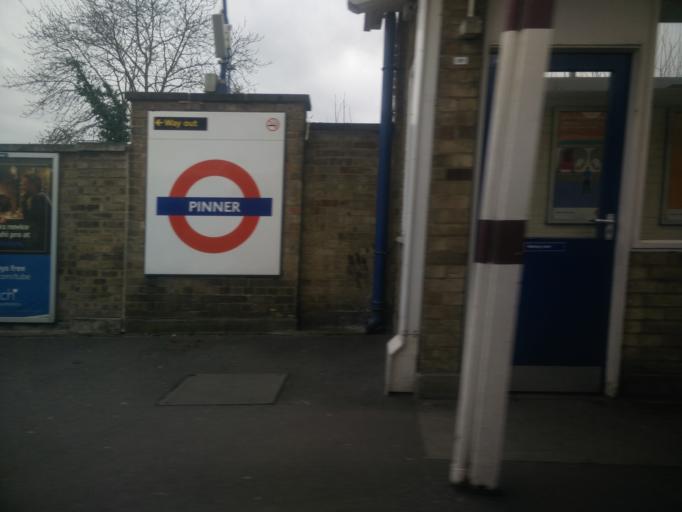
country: GB
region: England
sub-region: Greater London
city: Pinner
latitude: 51.5927
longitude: -0.3809
